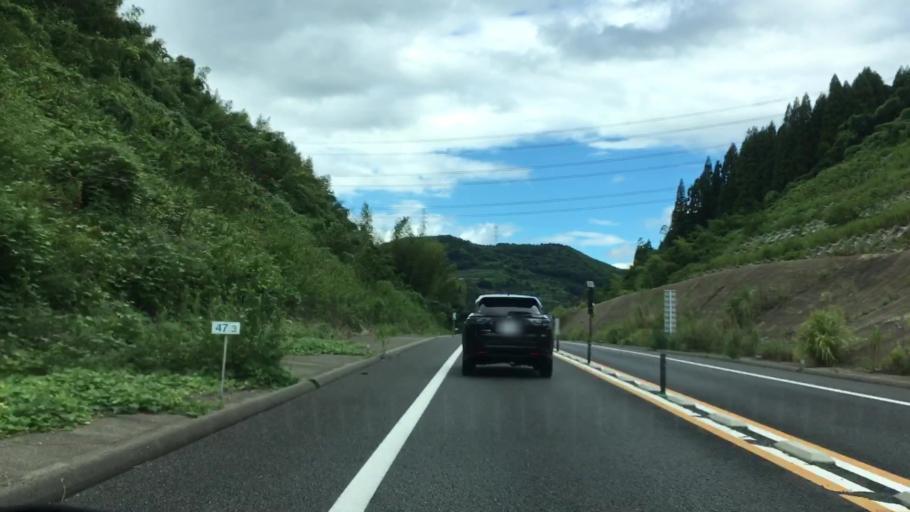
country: JP
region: Saga Prefecture
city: Karatsu
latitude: 33.3889
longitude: 129.9348
